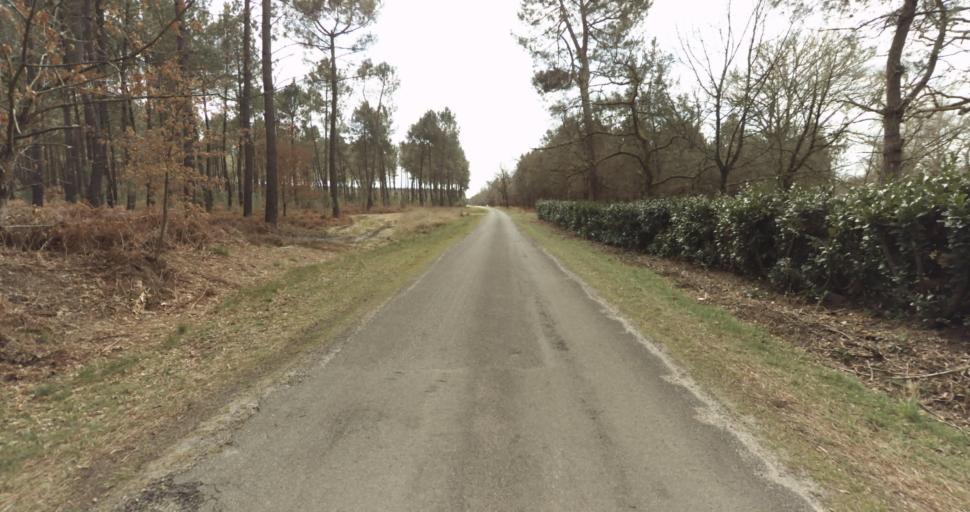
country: FR
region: Aquitaine
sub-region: Departement des Landes
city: Roquefort
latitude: 44.0568
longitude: -0.4292
